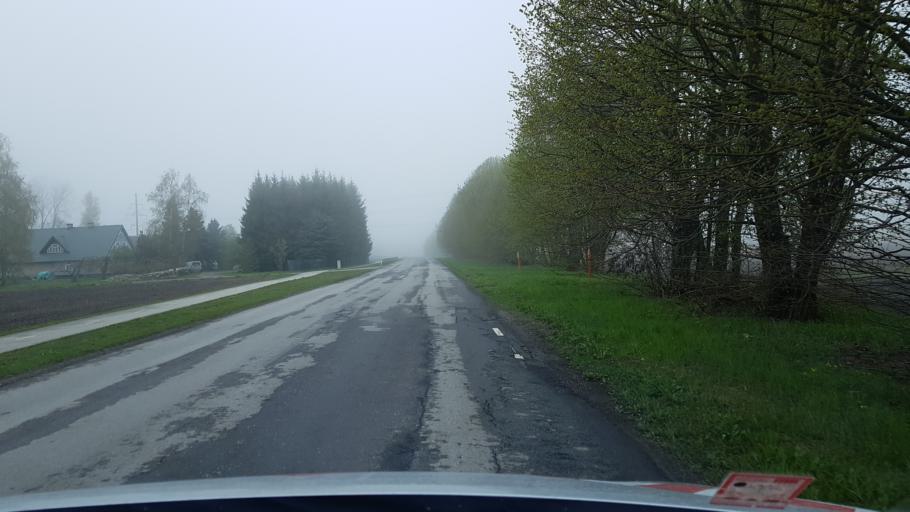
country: EE
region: Harju
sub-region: Joelaehtme vald
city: Loo
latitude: 59.4217
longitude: 24.9438
